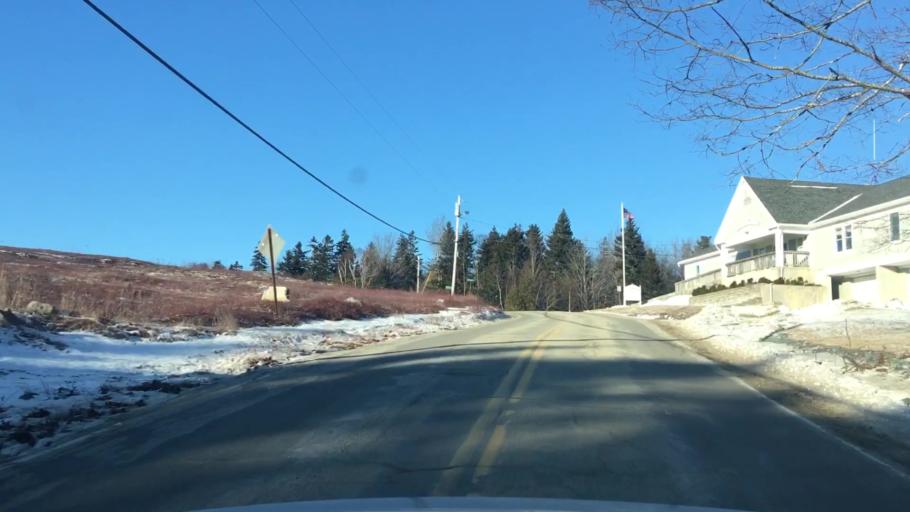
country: US
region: Maine
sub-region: Hancock County
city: Castine
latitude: 44.3631
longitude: -68.7501
